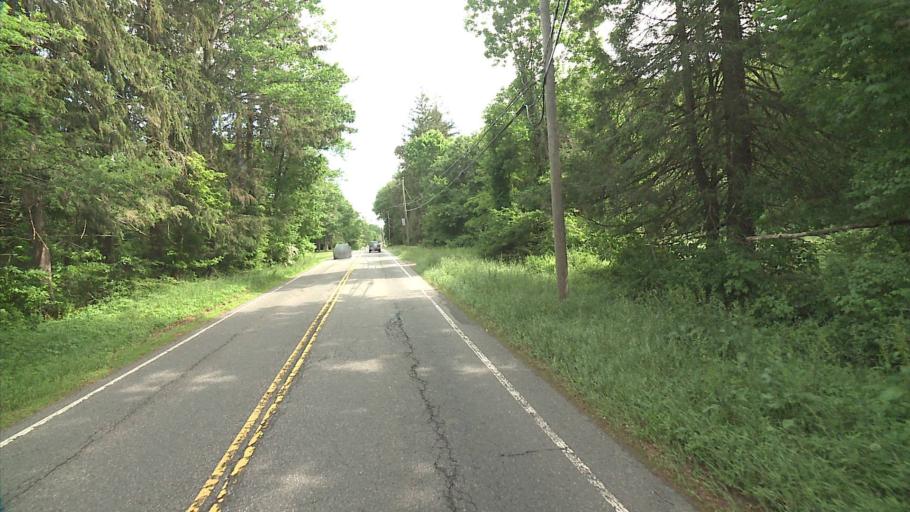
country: US
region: Connecticut
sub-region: Litchfield County
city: Litchfield
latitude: 41.7179
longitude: -73.1864
